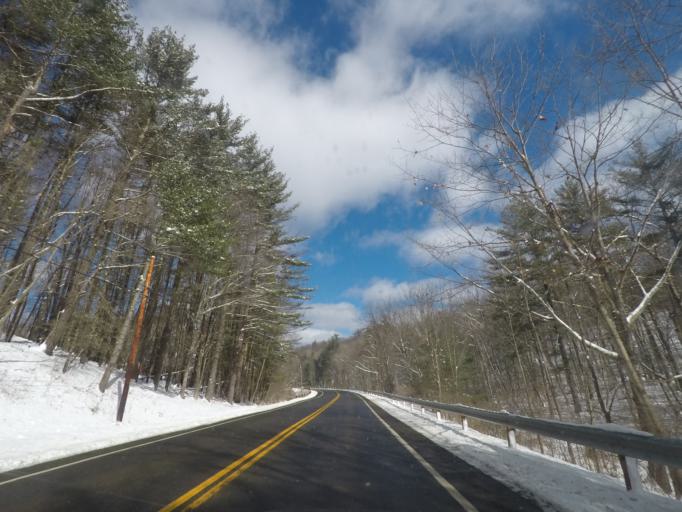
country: US
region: New York
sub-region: Rensselaer County
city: Nassau
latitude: 42.4719
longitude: -73.5250
